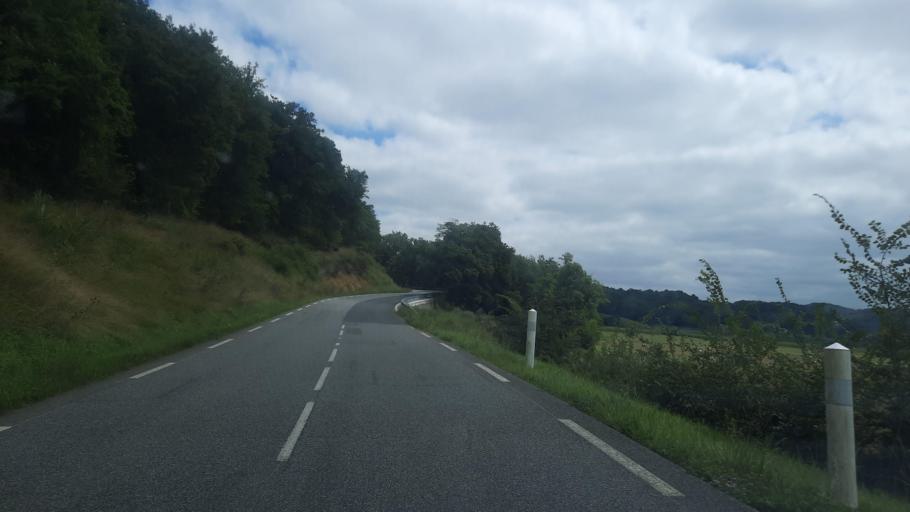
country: FR
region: Midi-Pyrenees
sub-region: Departement des Hautes-Pyrenees
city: Trie-sur-Baise
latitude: 43.3004
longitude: 0.2727
